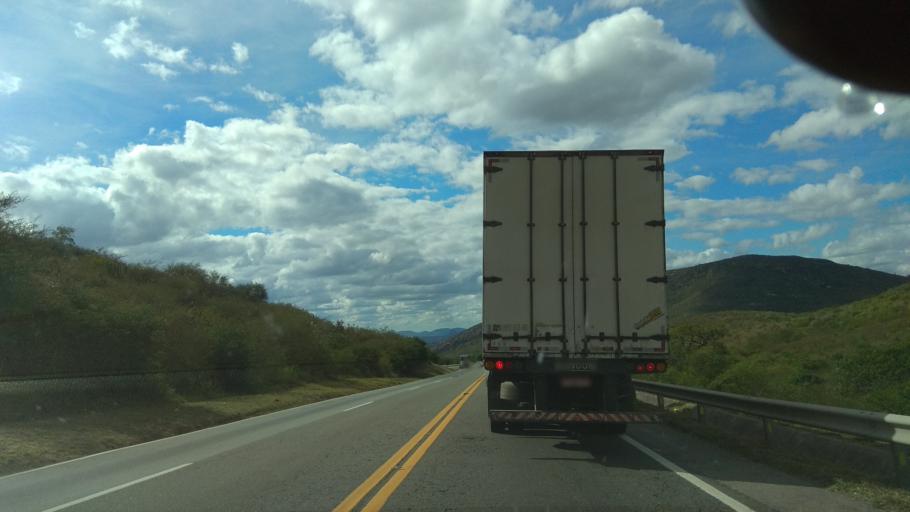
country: BR
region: Bahia
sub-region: Amargosa
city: Amargosa
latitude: -12.8916
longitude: -39.8594
